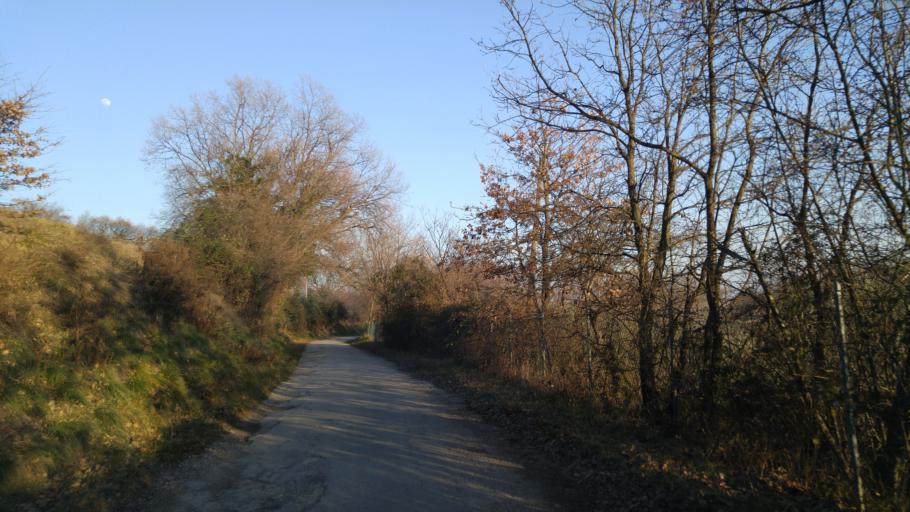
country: IT
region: The Marches
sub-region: Provincia di Pesaro e Urbino
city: Fenile
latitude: 43.8576
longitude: 12.9569
